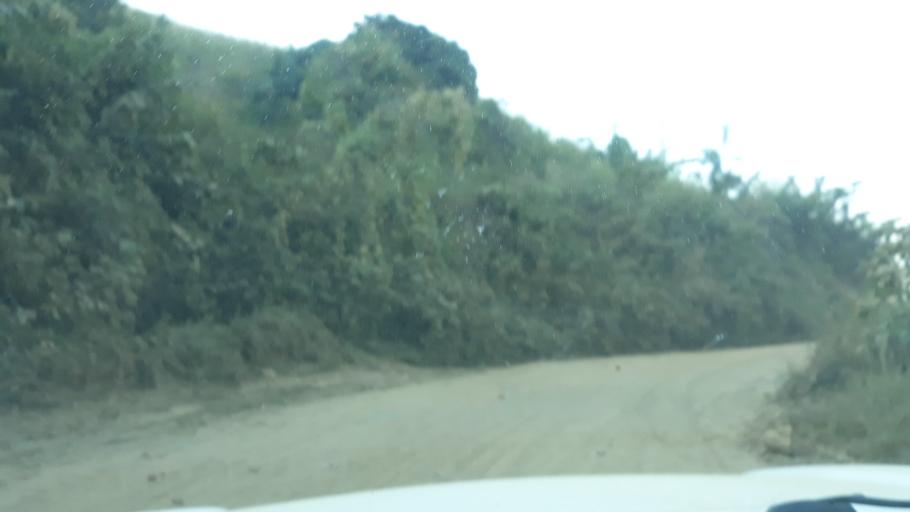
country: RW
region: Western Province
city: Cyangugu
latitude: -2.7043
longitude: 28.9523
